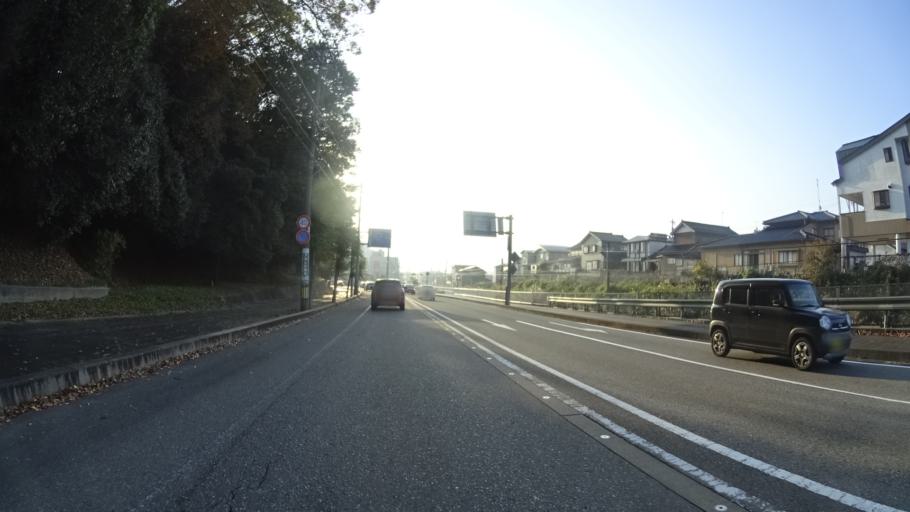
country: JP
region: Ishikawa
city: Nanao
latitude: 37.0459
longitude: 136.9592
